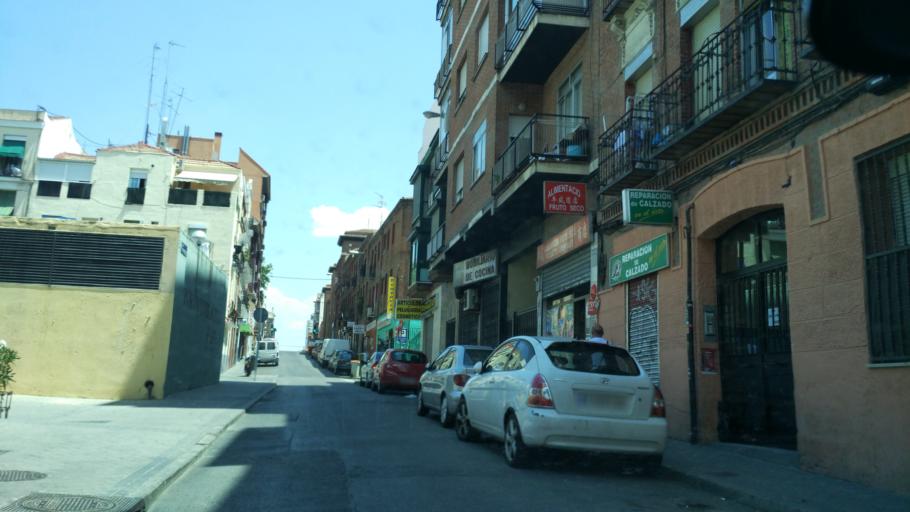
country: ES
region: Madrid
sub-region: Provincia de Madrid
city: Tetuan de las Victorias
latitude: 40.4529
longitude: -3.7045
